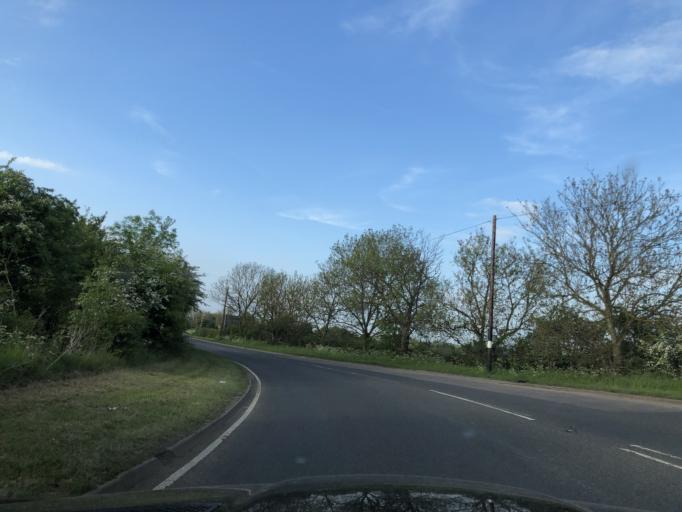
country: GB
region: England
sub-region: Warwickshire
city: Shipston on Stour
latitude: 52.0974
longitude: -1.6284
